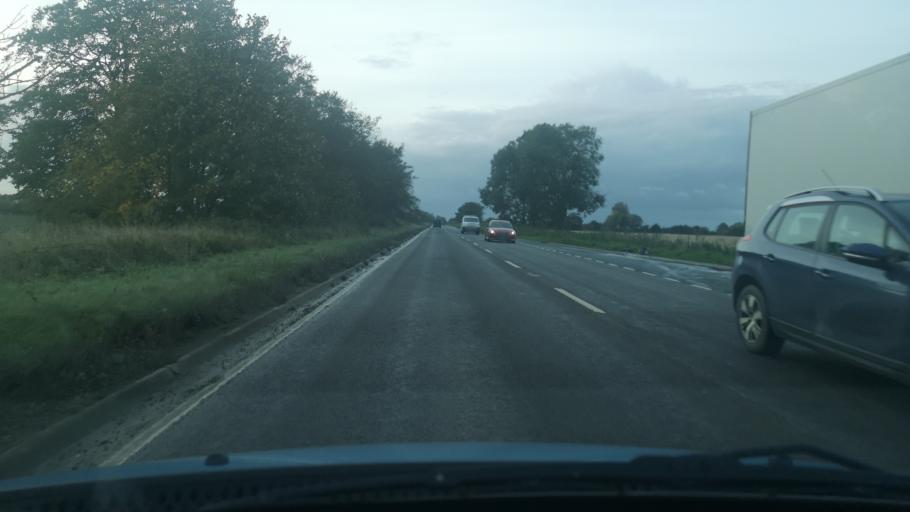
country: GB
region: England
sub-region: North Lincolnshire
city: Crowle
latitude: 53.5812
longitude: -0.8880
